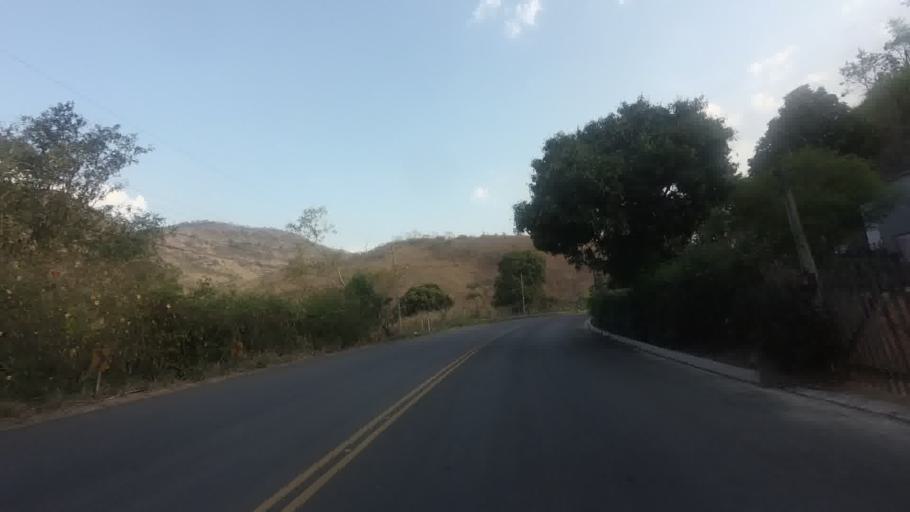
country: BR
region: Rio de Janeiro
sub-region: Cambuci
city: Cambuci
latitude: -21.4538
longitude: -42.0130
